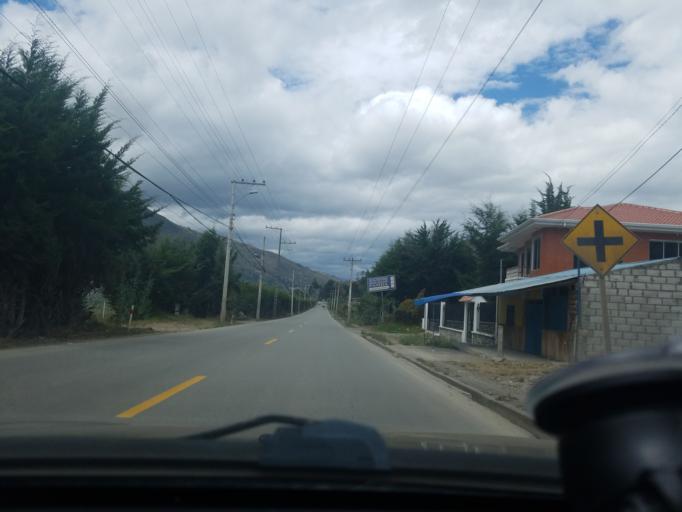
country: EC
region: Azuay
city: La Union
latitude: -2.8128
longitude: -78.7735
